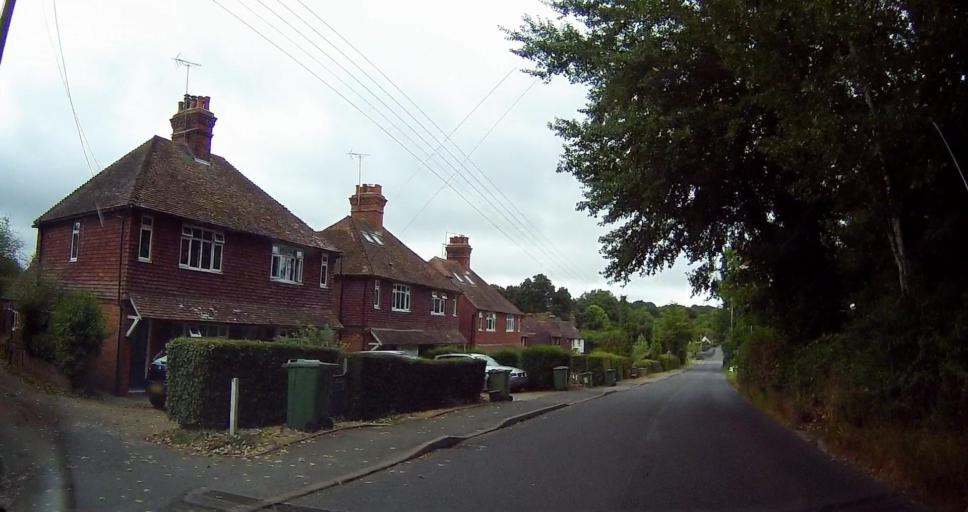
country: GB
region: England
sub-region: East Sussex
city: Wadhurst
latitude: 51.0925
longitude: 0.3875
